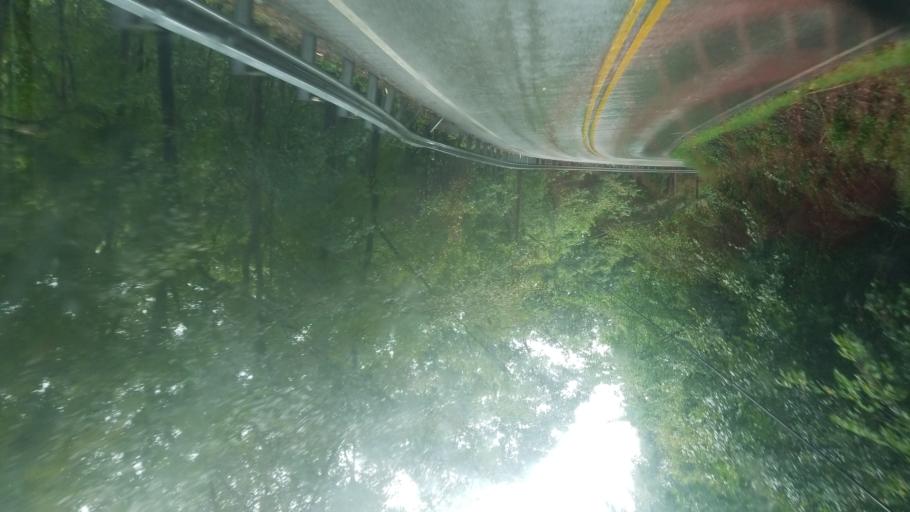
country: US
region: Kentucky
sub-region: Greenup County
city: South Shore
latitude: 38.6634
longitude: -82.9175
